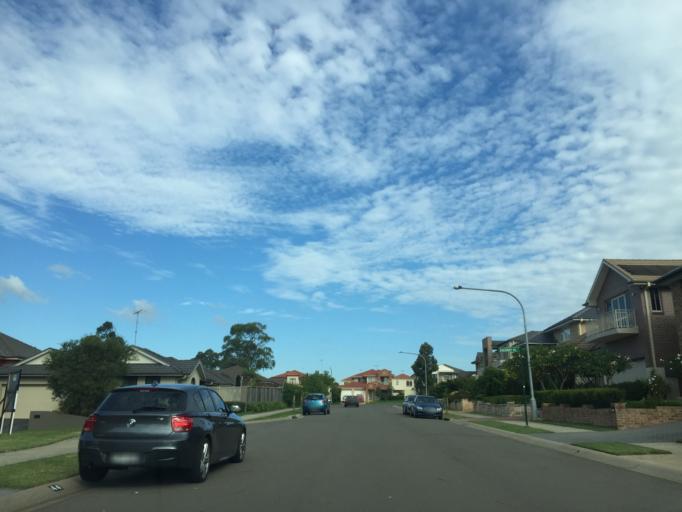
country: AU
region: New South Wales
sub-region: The Hills Shire
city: Beaumont Hills
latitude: -33.7094
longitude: 150.9703
